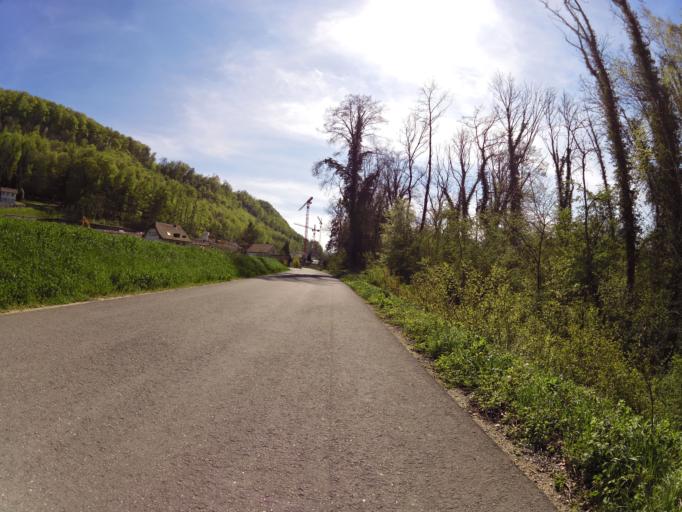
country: CH
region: Solothurn
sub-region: Bezirk Goesgen
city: Niedererlinsbach
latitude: 47.3843
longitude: 8.0215
